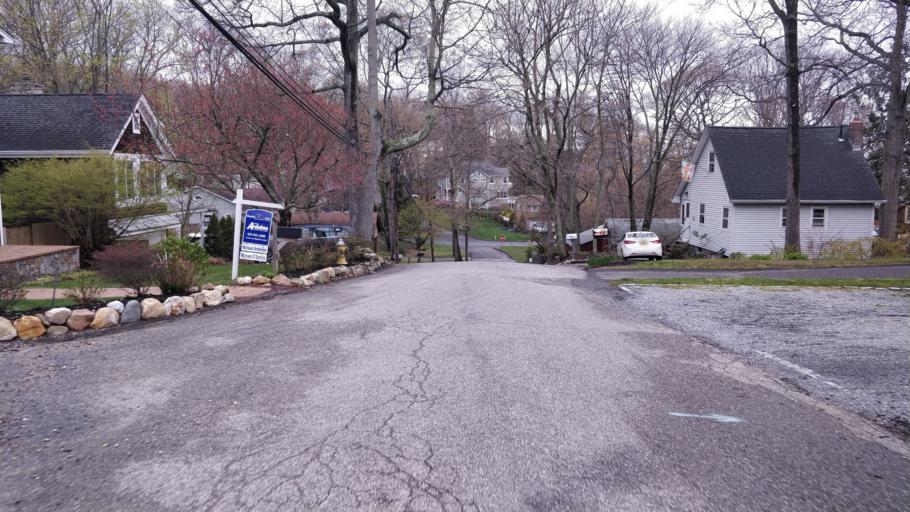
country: US
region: New York
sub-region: Suffolk County
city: Port Jefferson
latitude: 40.9517
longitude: -73.0815
